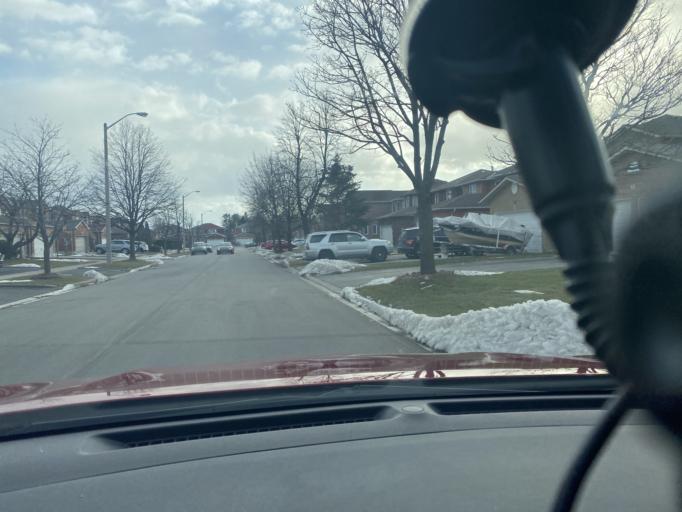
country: CA
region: Ontario
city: Scarborough
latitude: 43.7961
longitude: -79.1614
